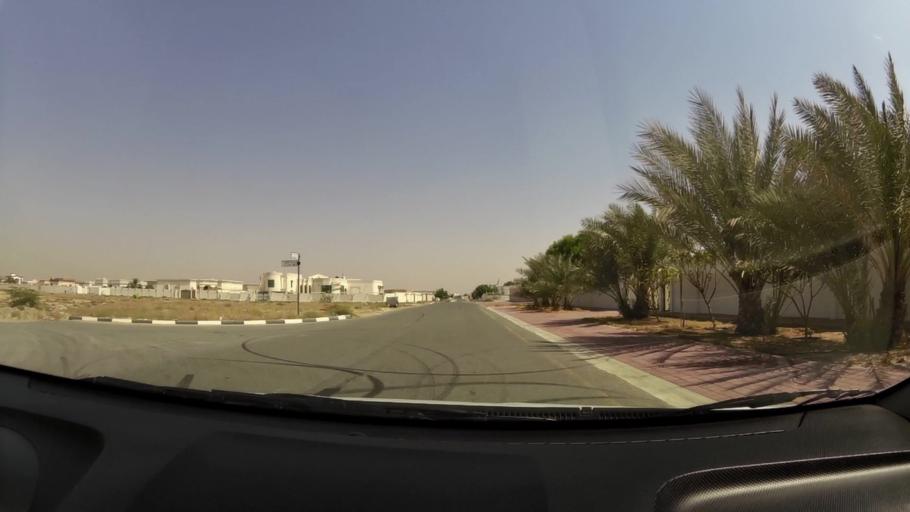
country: AE
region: Umm al Qaywayn
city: Umm al Qaywayn
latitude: 25.4917
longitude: 55.5865
